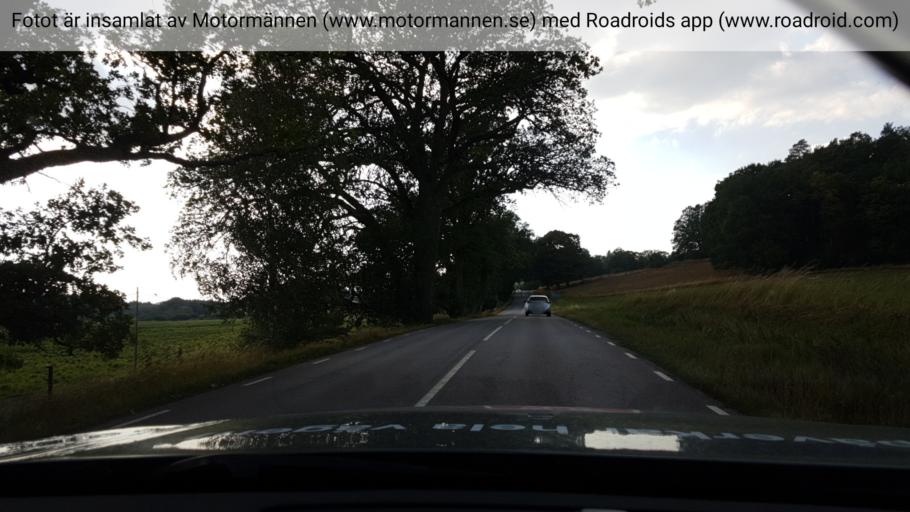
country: SE
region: Soedermanland
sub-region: Gnesta Kommun
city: Gnesta
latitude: 59.0780
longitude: 17.2816
